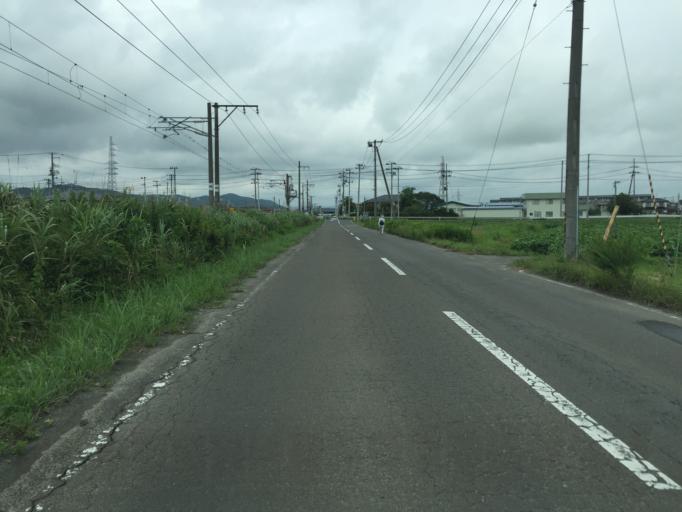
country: JP
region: Miyagi
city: Watari
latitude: 38.0323
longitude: 140.8669
